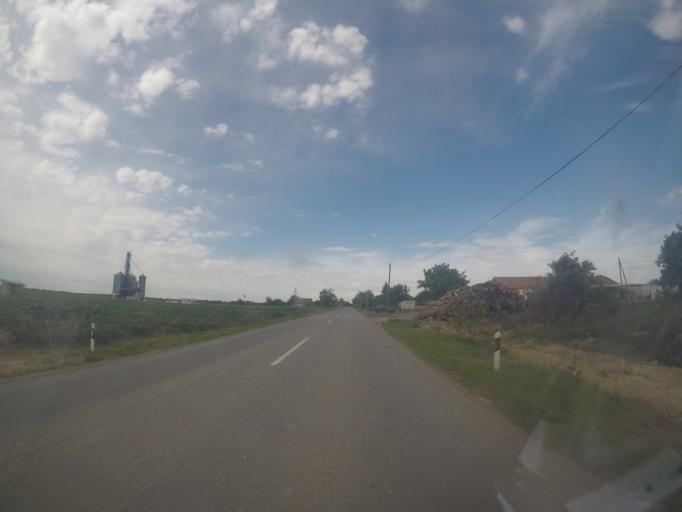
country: RS
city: Perlez
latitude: 45.2200
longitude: 20.3982
